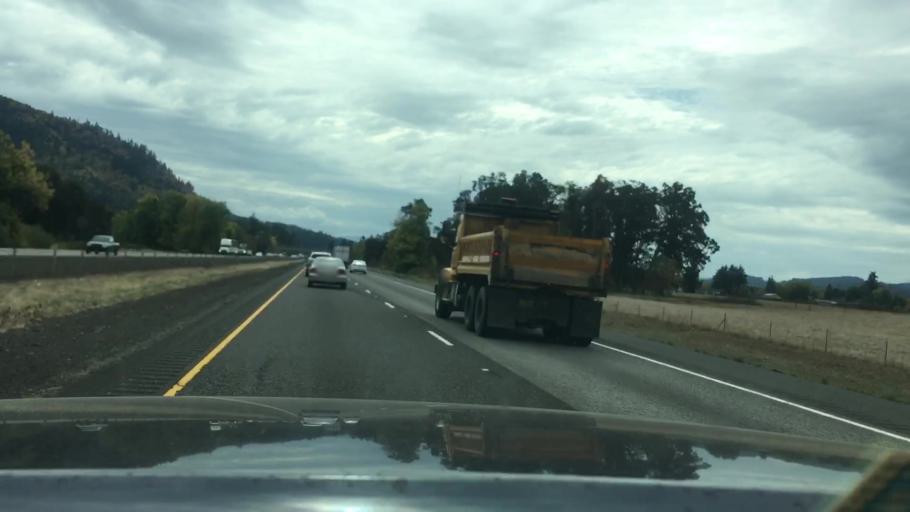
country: US
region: Oregon
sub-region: Lane County
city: Creswell
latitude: 43.8912
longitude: -123.0145
